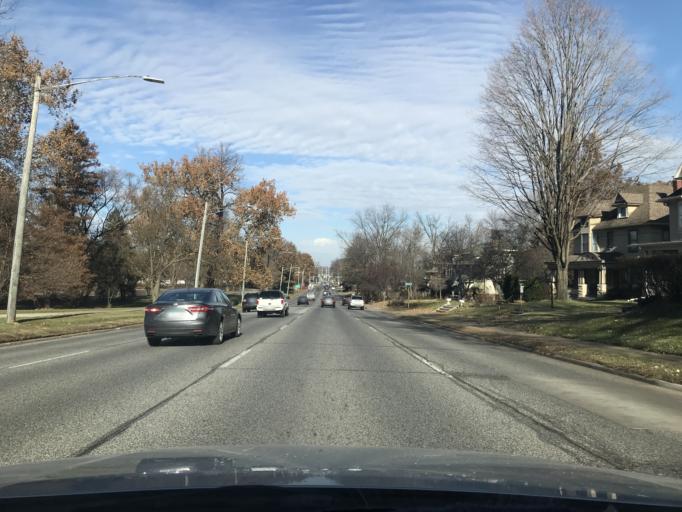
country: US
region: Iowa
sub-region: Scott County
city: Davenport
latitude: 41.5430
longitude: -90.5733
